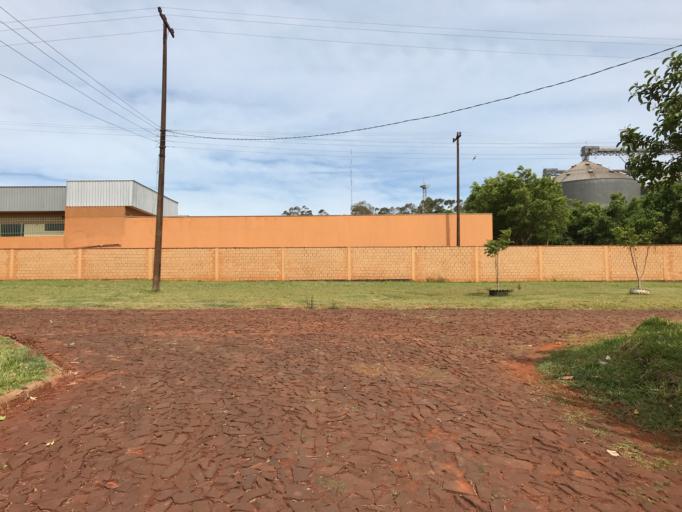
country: PY
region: Alto Parana
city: Naranjal
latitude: -25.9729
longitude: -55.2104
